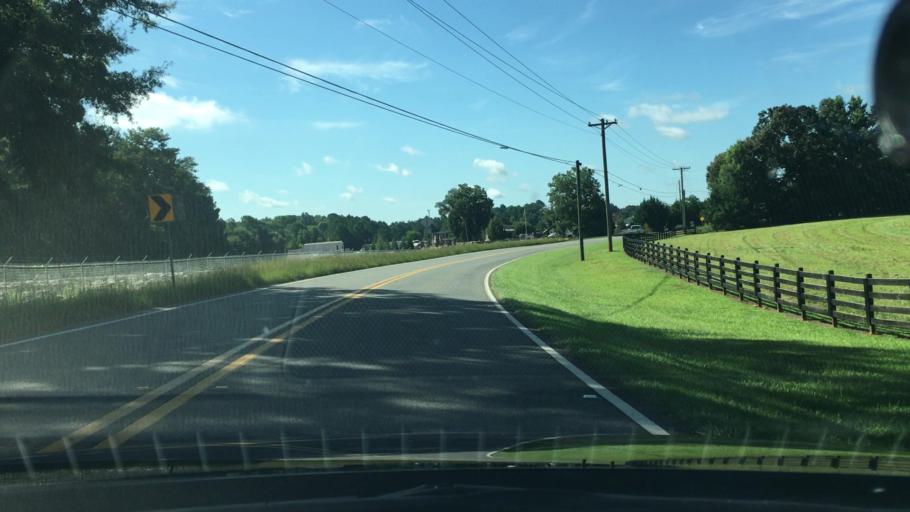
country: US
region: Georgia
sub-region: Putnam County
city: Jefferson
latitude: 33.4418
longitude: -83.2818
